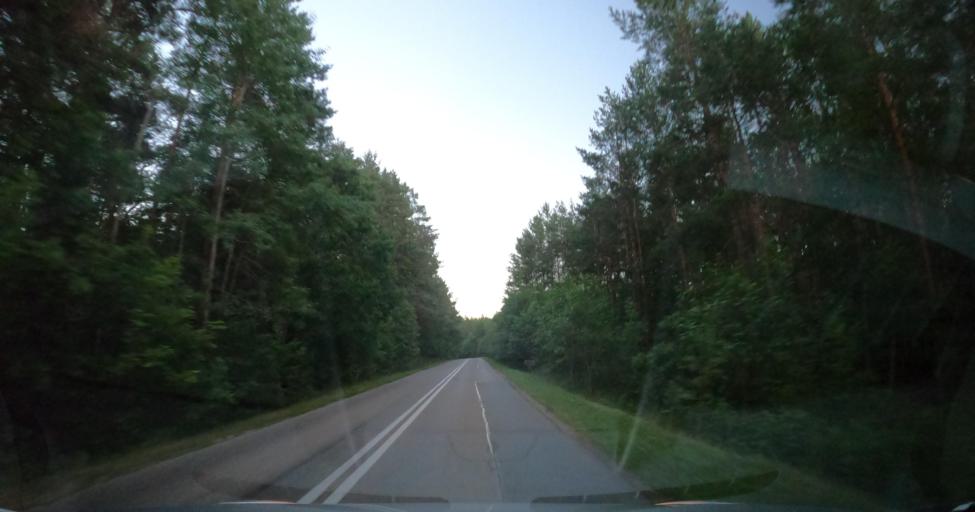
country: PL
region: Pomeranian Voivodeship
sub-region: Powiat wejherowski
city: Linia
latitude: 54.4665
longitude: 17.9907
